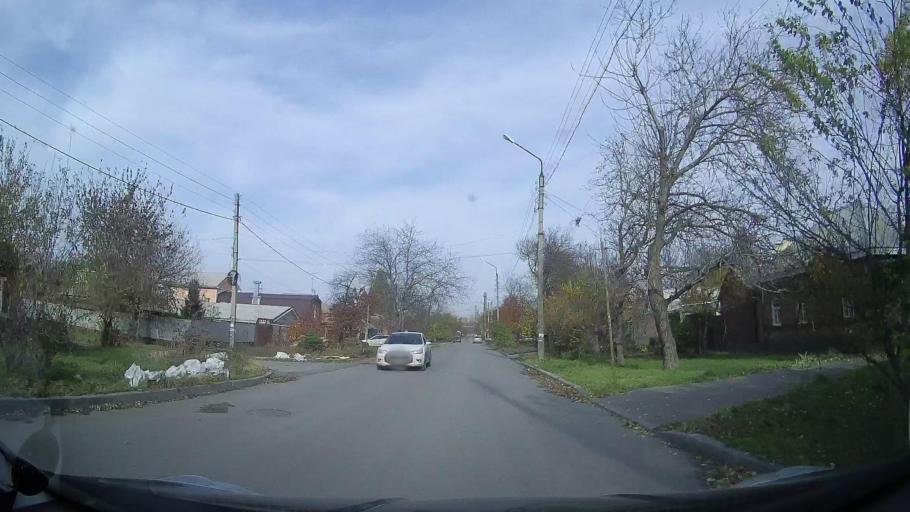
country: RU
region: Rostov
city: Severnyy
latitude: 47.2622
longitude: 39.7231
